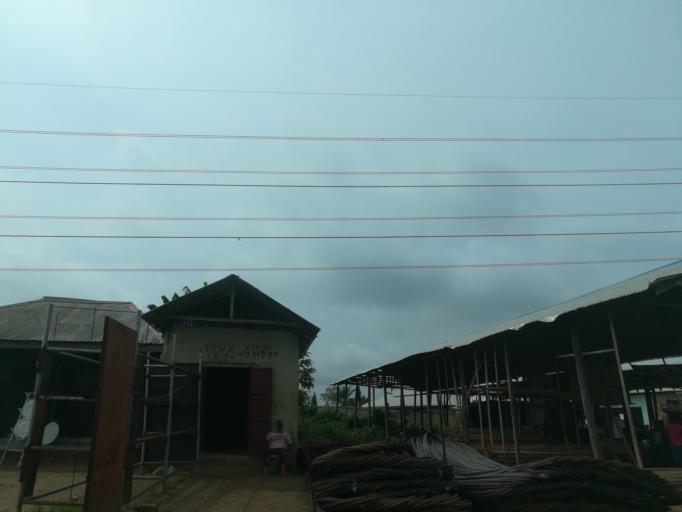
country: NG
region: Rivers
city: Emuoha
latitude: 4.8932
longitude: 6.9716
